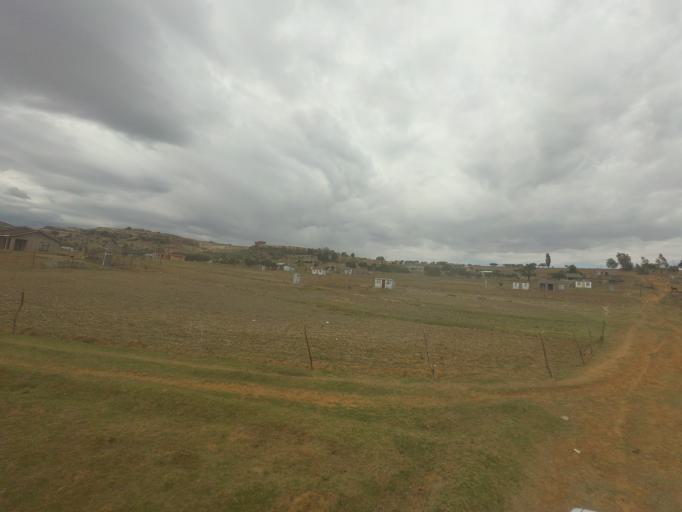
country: LS
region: Leribe
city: Leribe
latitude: -29.0259
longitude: 28.0207
